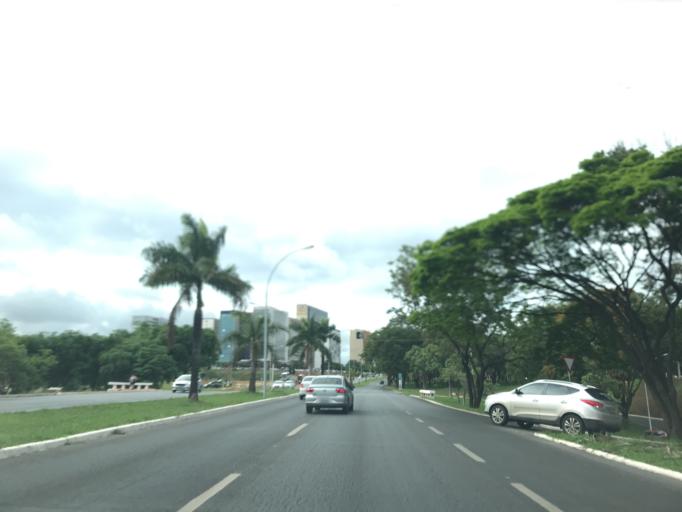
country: BR
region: Federal District
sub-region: Brasilia
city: Brasilia
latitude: -15.7829
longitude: -47.8800
